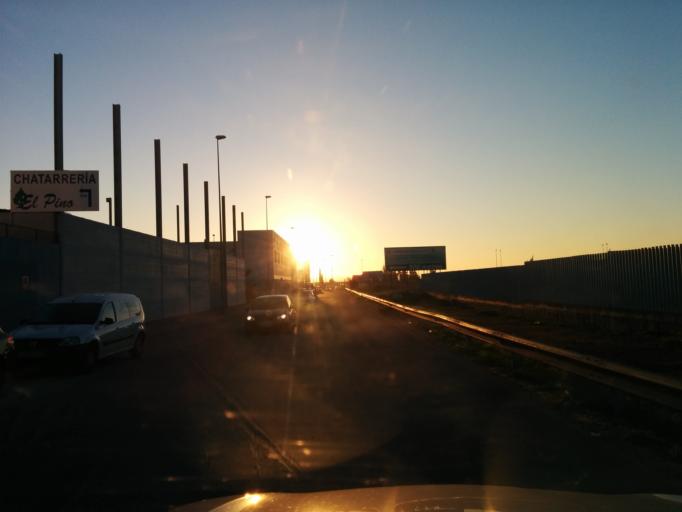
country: ES
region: Andalusia
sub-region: Provincia de Sevilla
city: Sevilla
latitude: 37.3736
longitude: -5.9274
